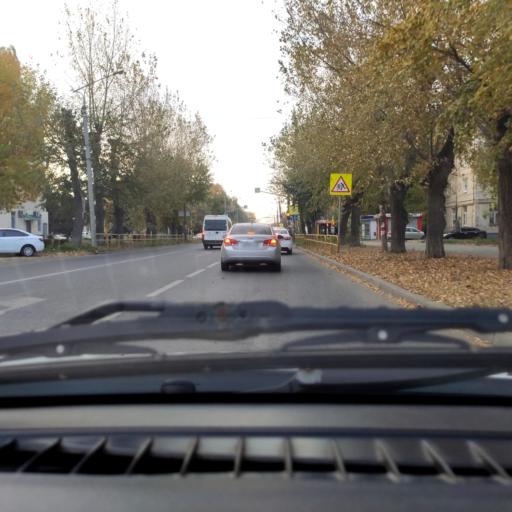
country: RU
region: Samara
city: Tol'yatti
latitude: 53.5315
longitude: 49.4117
